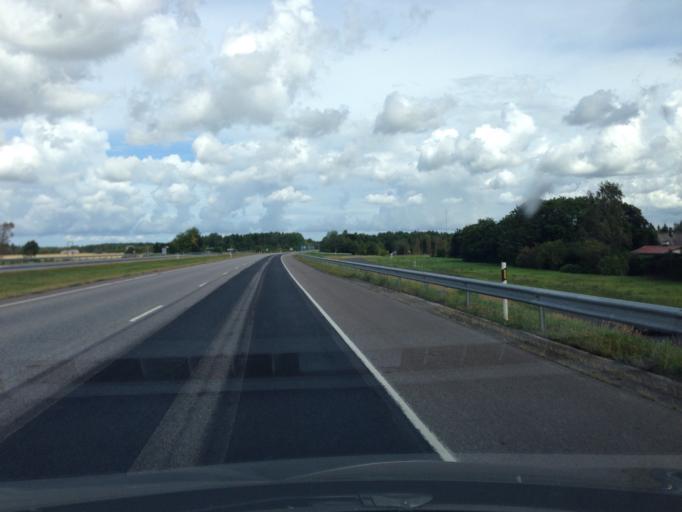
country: EE
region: Harju
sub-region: Saue linn
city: Saue
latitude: 59.2750
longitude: 24.5230
